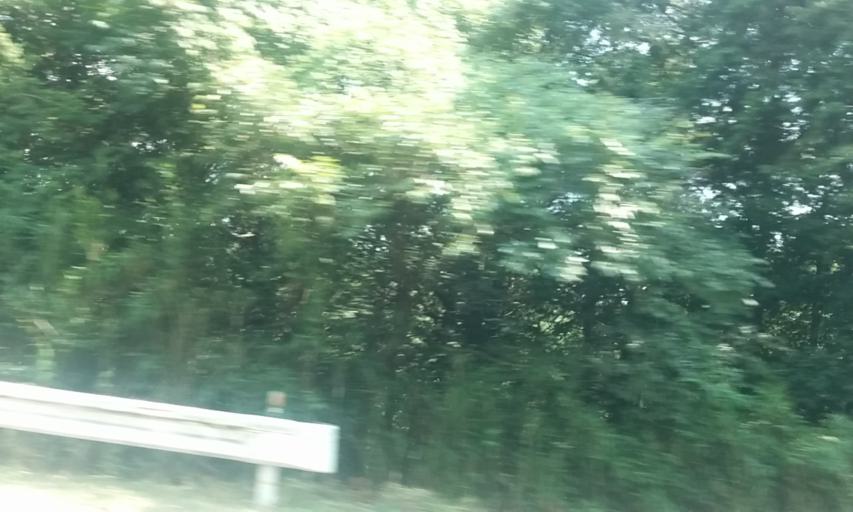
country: JP
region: Kyoto
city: Fukuchiyama
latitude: 35.2682
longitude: 135.1461
